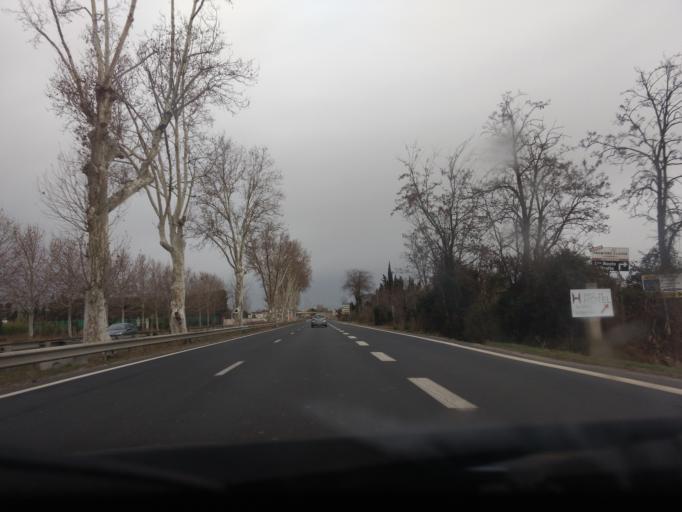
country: FR
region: Languedoc-Roussillon
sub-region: Departement de l'Herault
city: Lattes
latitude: 43.5766
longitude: 3.8975
